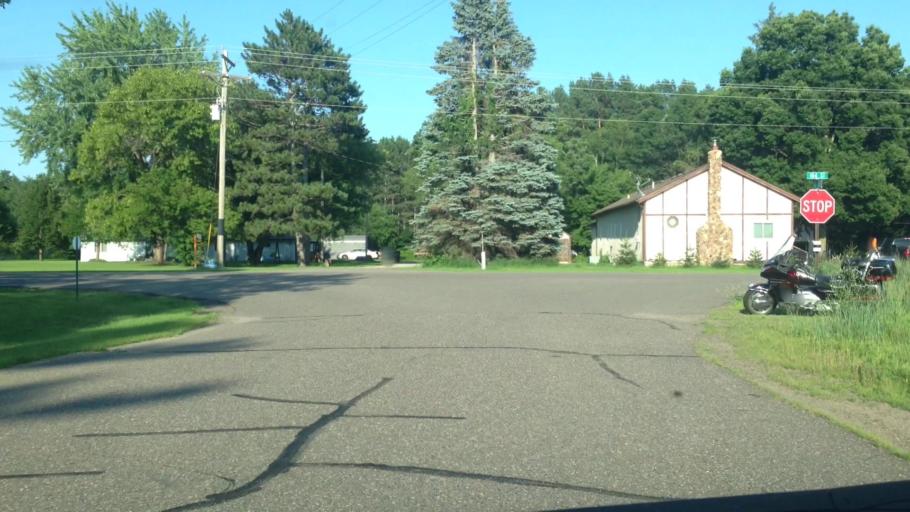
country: US
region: Minnesota
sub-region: Sherburne County
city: Big Lake
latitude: 45.4440
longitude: -93.7364
